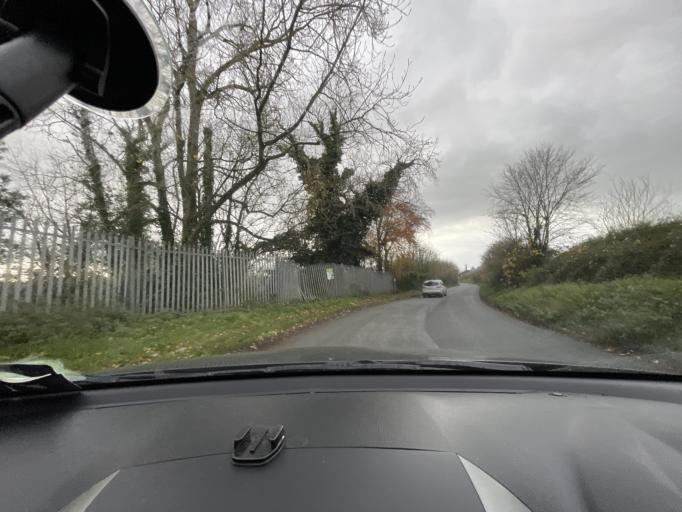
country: IE
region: Leinster
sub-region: Lu
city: Drogheda
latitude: 53.7225
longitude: -6.3222
